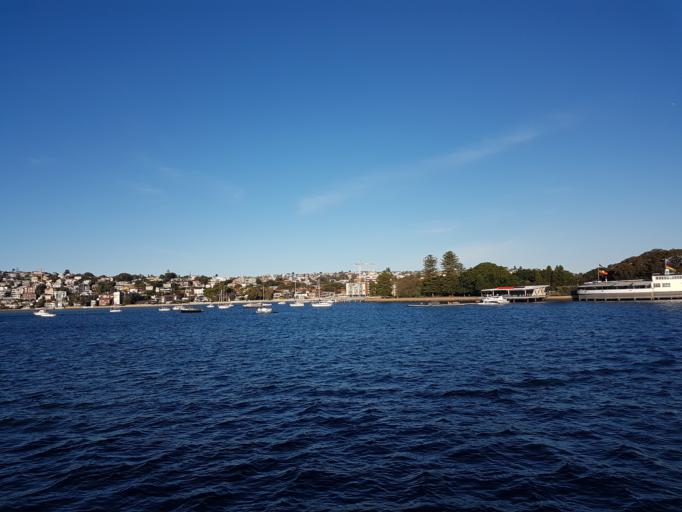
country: AU
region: New South Wales
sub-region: Woollahra
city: Point Piper
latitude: -33.8691
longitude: 151.2607
